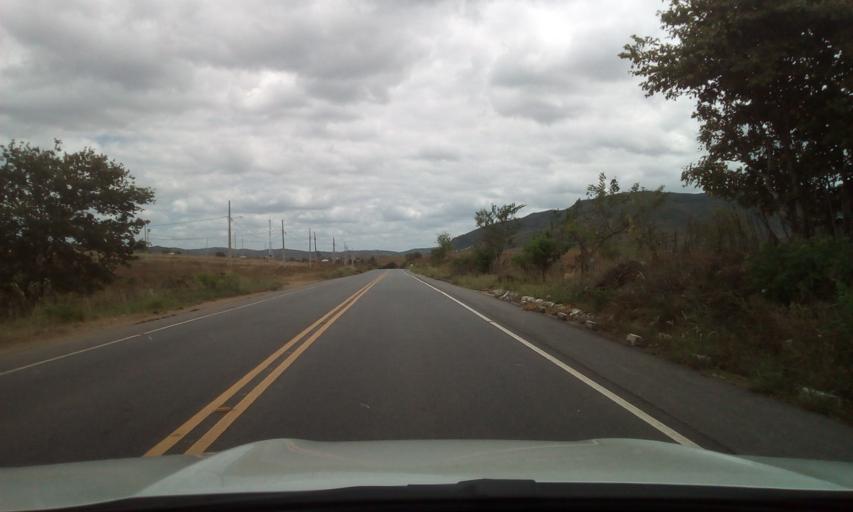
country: BR
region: Paraiba
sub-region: Serra Redonda
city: Alagoa Grande
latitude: -7.1914
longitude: -35.5880
